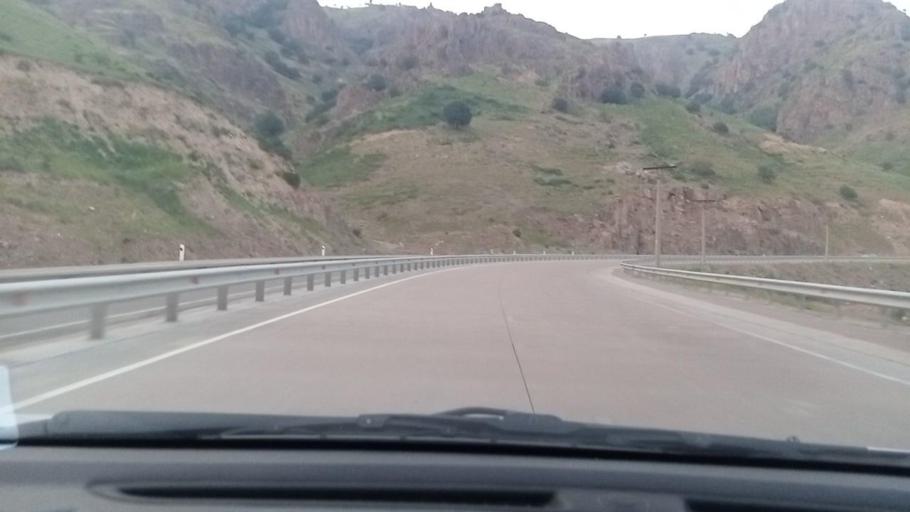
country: UZ
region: Toshkent
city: Angren
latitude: 41.1358
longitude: 70.3732
